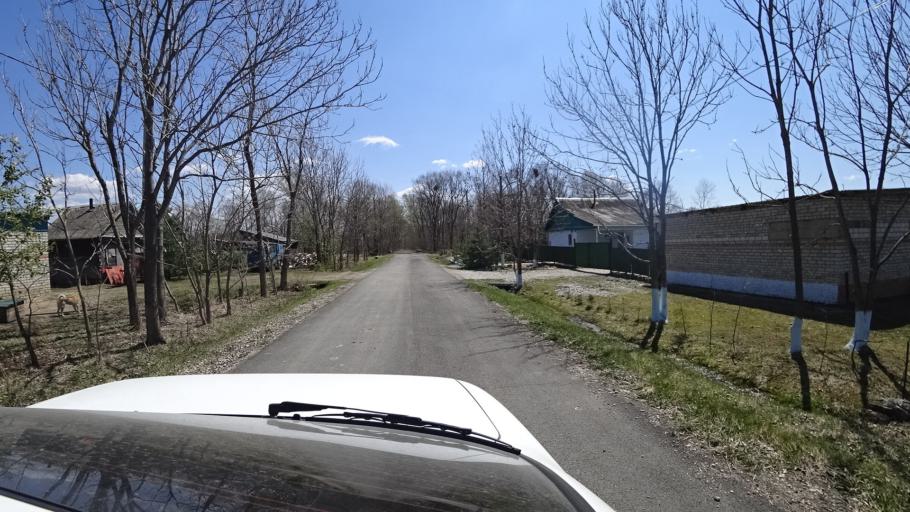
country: RU
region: Primorskiy
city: Dal'nerechensk
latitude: 45.7913
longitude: 133.7730
